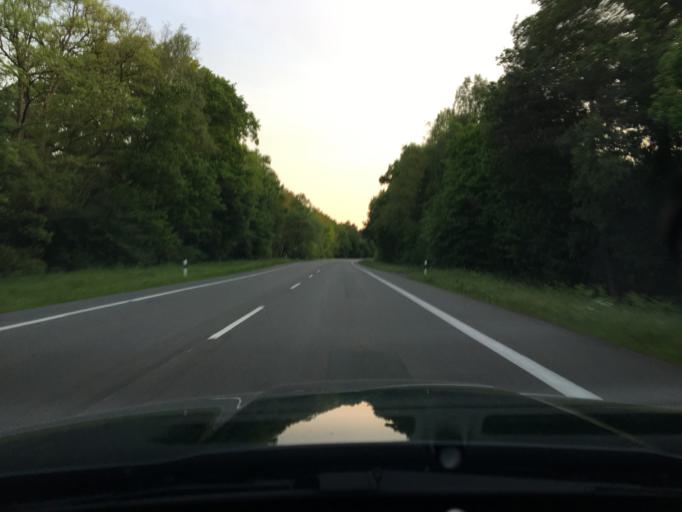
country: DE
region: North Rhine-Westphalia
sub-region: Regierungsbezirk Munster
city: Ladbergen
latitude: 52.1511
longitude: 7.7747
